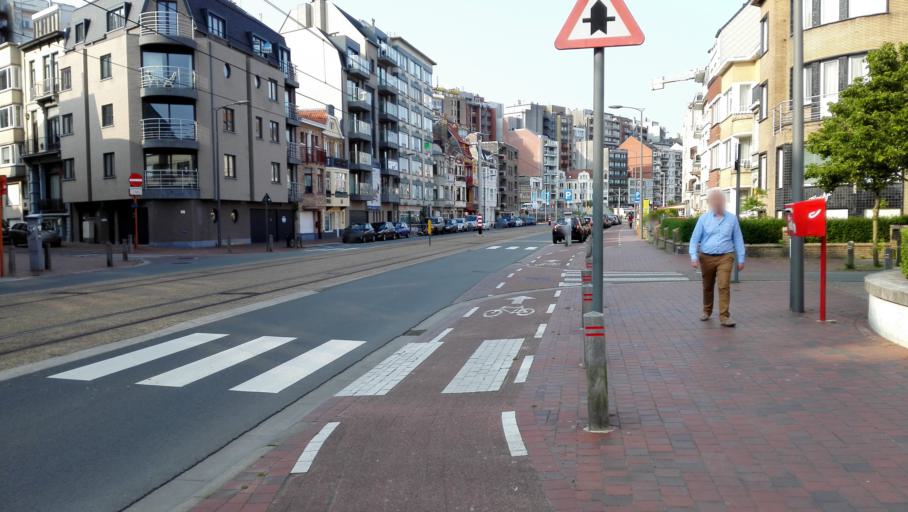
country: BE
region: Flanders
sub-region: Provincie West-Vlaanderen
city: Blankenberge
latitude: 51.3161
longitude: 3.1343
